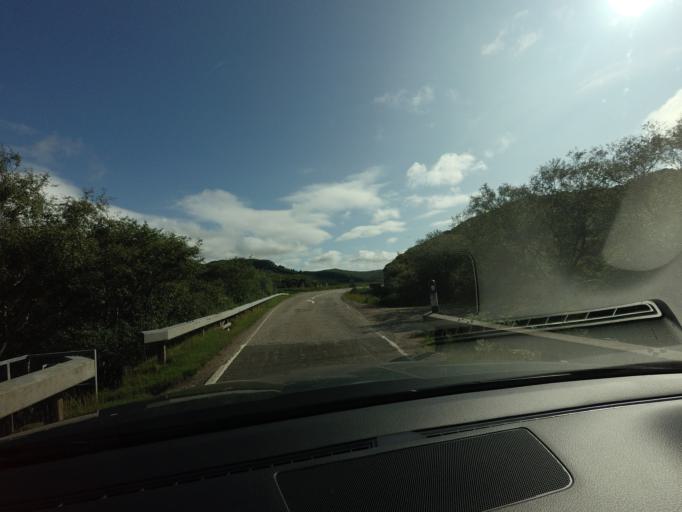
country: GB
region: Scotland
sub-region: Highland
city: Ullapool
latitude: 58.3746
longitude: -5.0168
